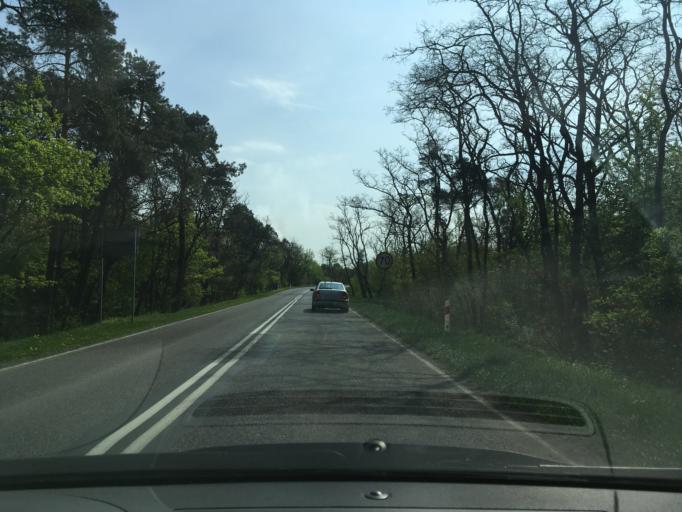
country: PL
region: Lublin Voivodeship
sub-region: Powiat pulawski
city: Pulawy
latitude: 51.4615
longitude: 21.9422
